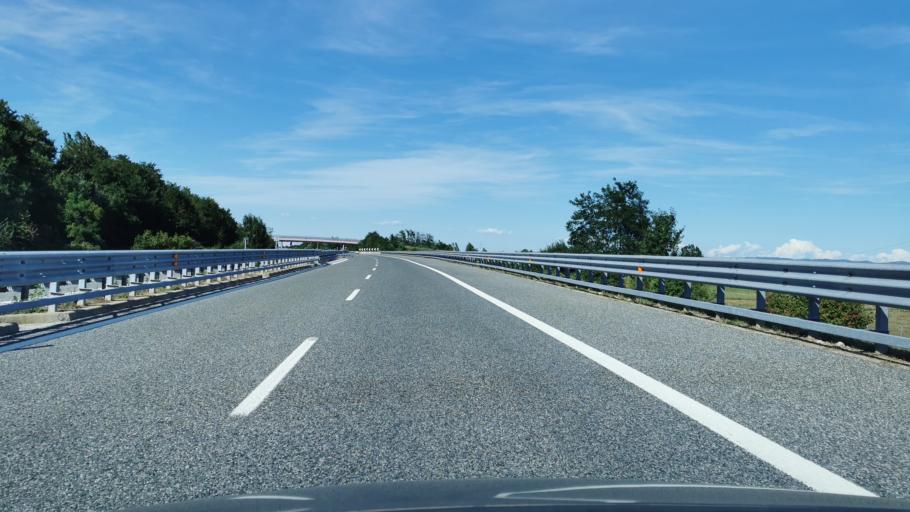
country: IT
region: Piedmont
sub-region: Provincia di Cuneo
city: Magliano Alpi
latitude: 44.4727
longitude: 7.7871
